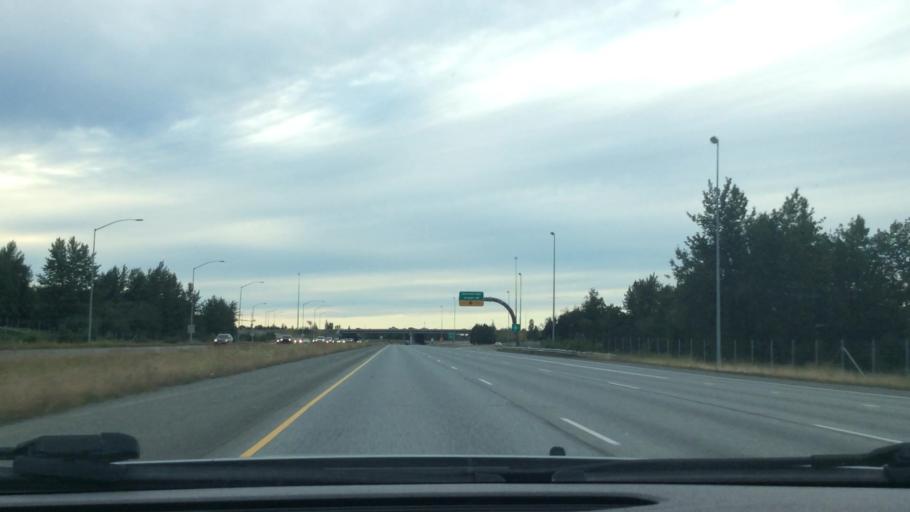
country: US
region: Alaska
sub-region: Anchorage Municipality
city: Anchorage
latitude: 61.1674
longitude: -149.9155
